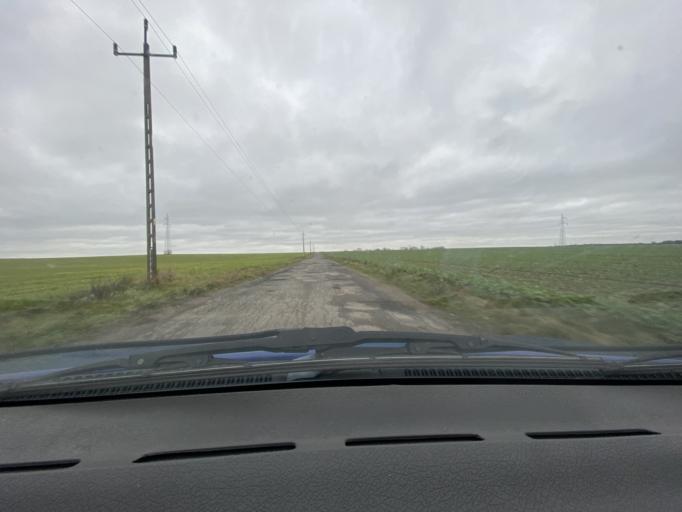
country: PL
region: West Pomeranian Voivodeship
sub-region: Powiat gryficki
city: Gryfice
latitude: 53.9552
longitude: 15.2572
